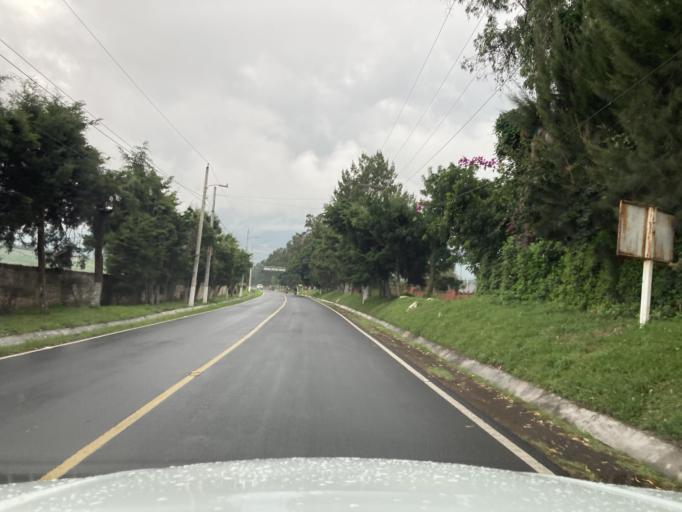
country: GT
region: Sacatepequez
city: San Miguel Duenas
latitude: 14.5215
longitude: -90.7916
